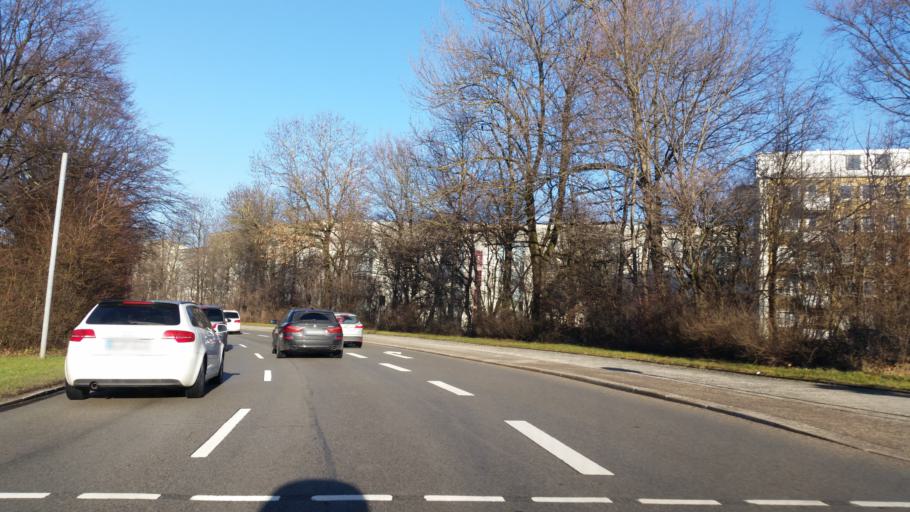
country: DE
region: Bavaria
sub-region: Upper Bavaria
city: Bogenhausen
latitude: 48.1248
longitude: 11.6207
